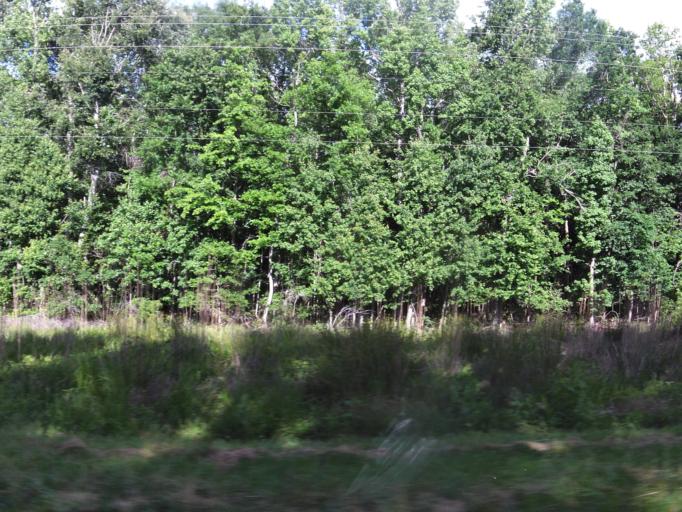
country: US
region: South Carolina
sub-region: Allendale County
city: Fairfax
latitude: 32.9158
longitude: -81.2375
